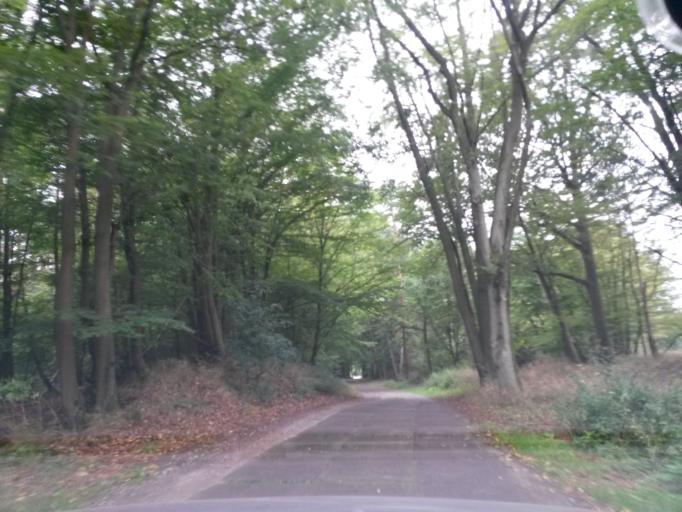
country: DE
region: Brandenburg
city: Althuttendorf
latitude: 53.0823
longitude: 13.8373
